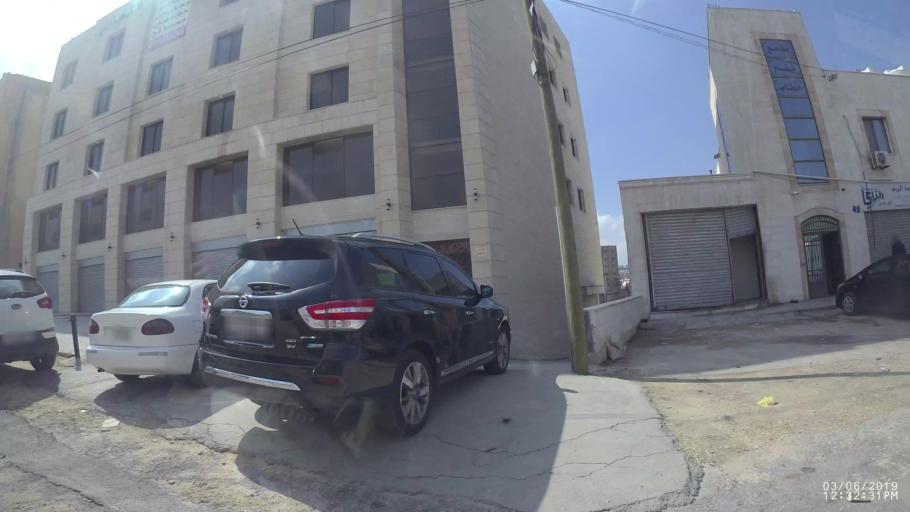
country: JO
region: Zarqa
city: Russeifa
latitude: 31.9944
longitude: 35.9952
